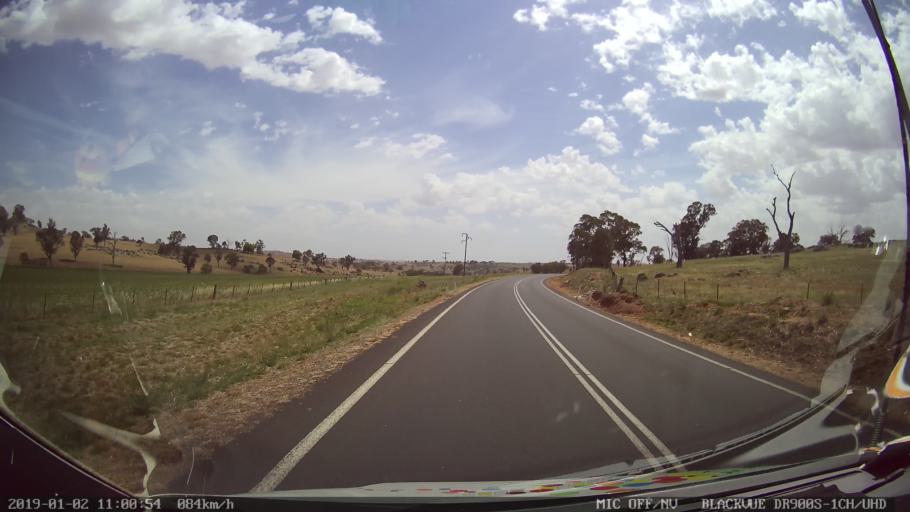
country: AU
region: New South Wales
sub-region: Cootamundra
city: Cootamundra
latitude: -34.6031
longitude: 148.3146
